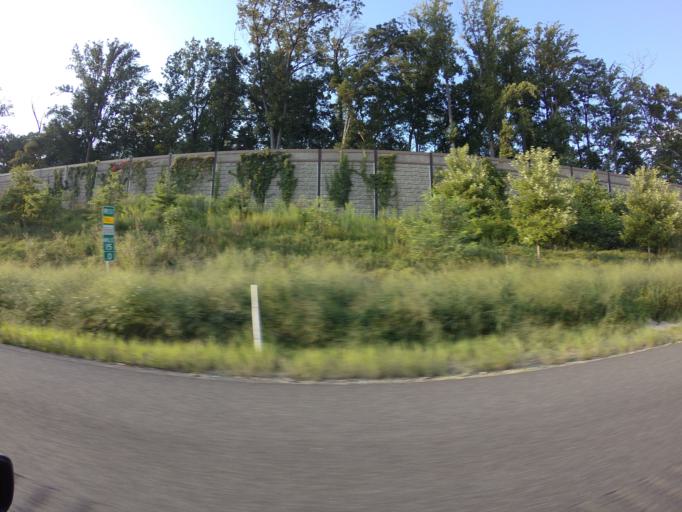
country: US
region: Maryland
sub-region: Montgomery County
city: Fairland
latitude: 39.0834
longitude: -76.9688
